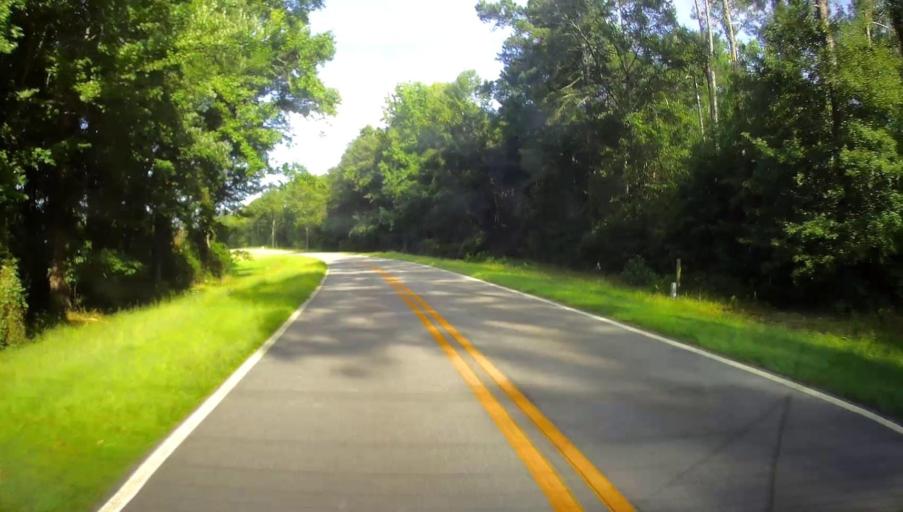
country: US
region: Georgia
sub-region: Crawford County
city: Knoxville
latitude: 32.7562
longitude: -83.9367
